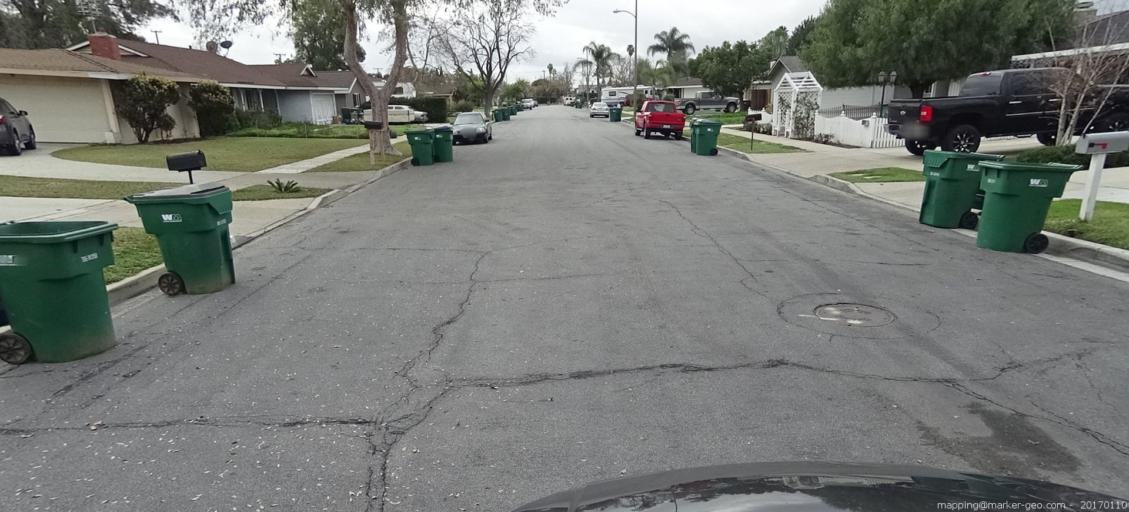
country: US
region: California
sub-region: Orange County
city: Tustin
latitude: 33.7700
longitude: -117.8281
